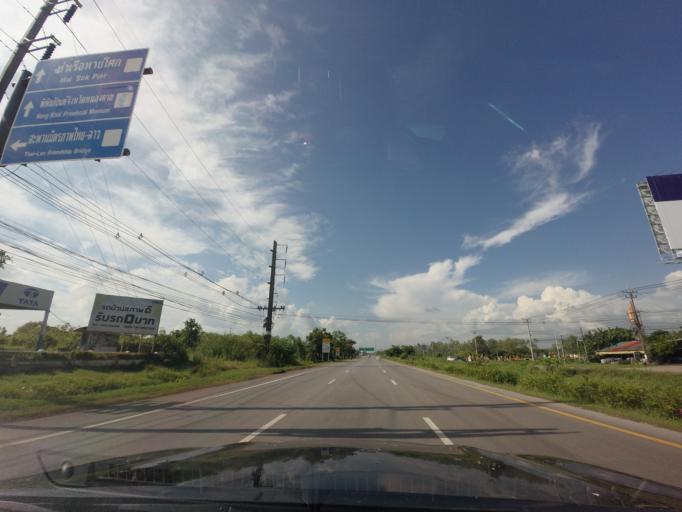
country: TH
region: Nong Khai
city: Nong Khai
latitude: 17.8087
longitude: 102.7599
